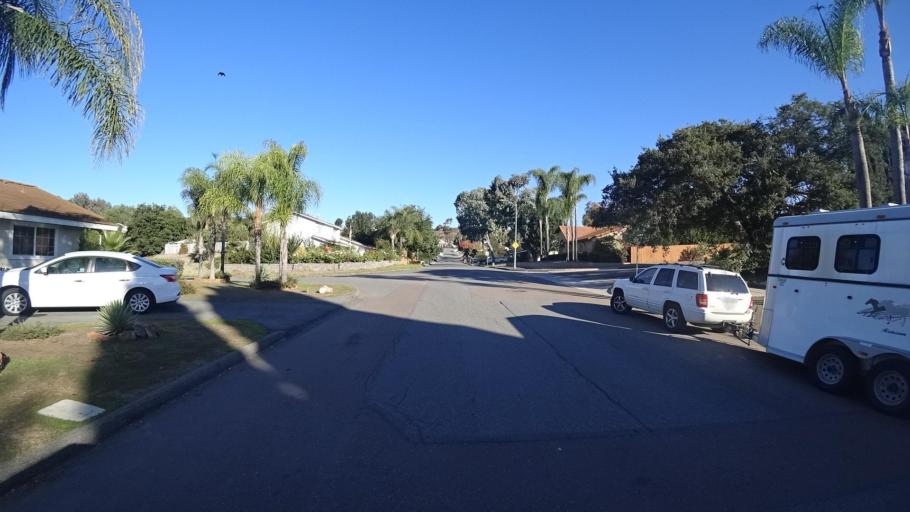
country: US
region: California
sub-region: San Diego County
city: Bonita
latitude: 32.6726
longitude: -117.0300
